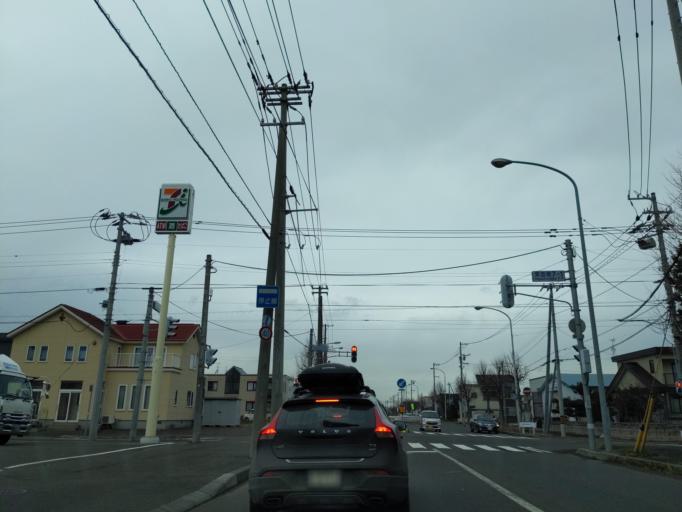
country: JP
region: Hokkaido
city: Sapporo
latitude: 43.0976
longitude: 141.4058
